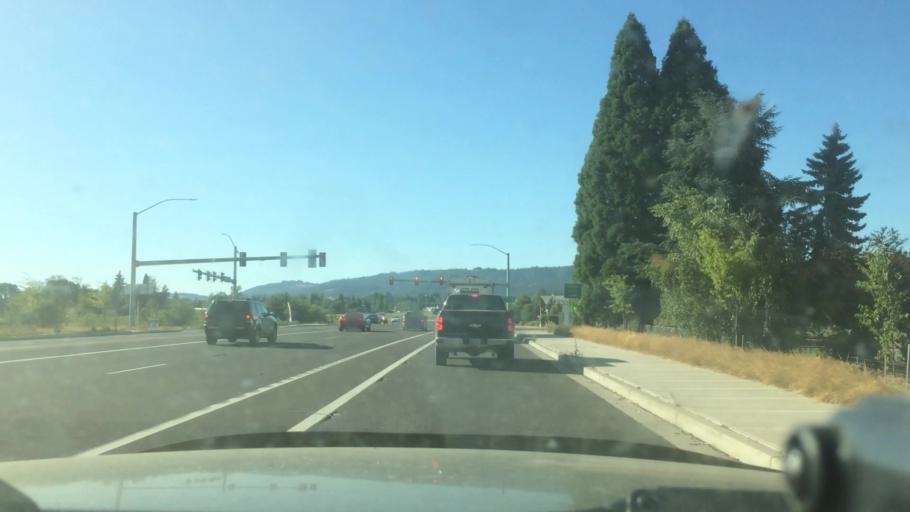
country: US
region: Oregon
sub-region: Yamhill County
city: Newberg
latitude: 45.2928
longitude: -122.9490
